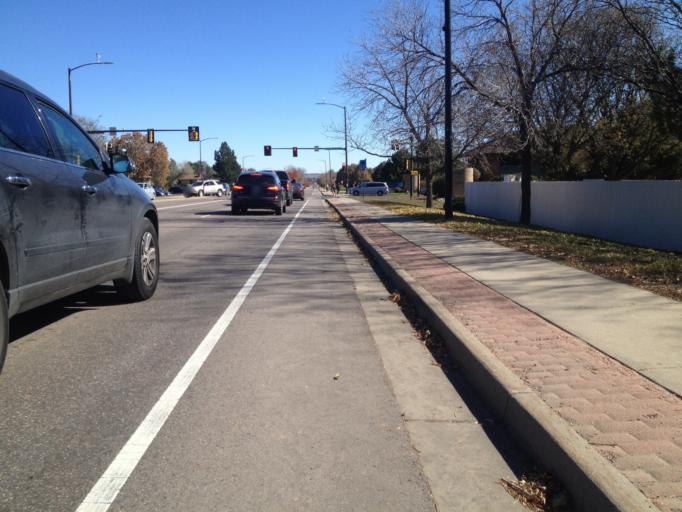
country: US
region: Colorado
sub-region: Boulder County
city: Lafayette
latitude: 39.9869
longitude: -105.1088
